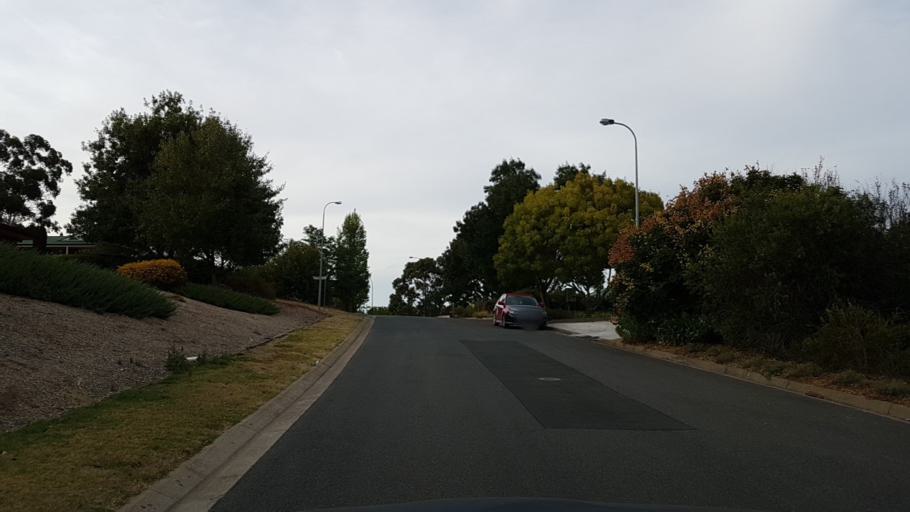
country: AU
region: South Australia
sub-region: Mount Barker
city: Nairne
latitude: -35.0273
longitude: 138.9093
